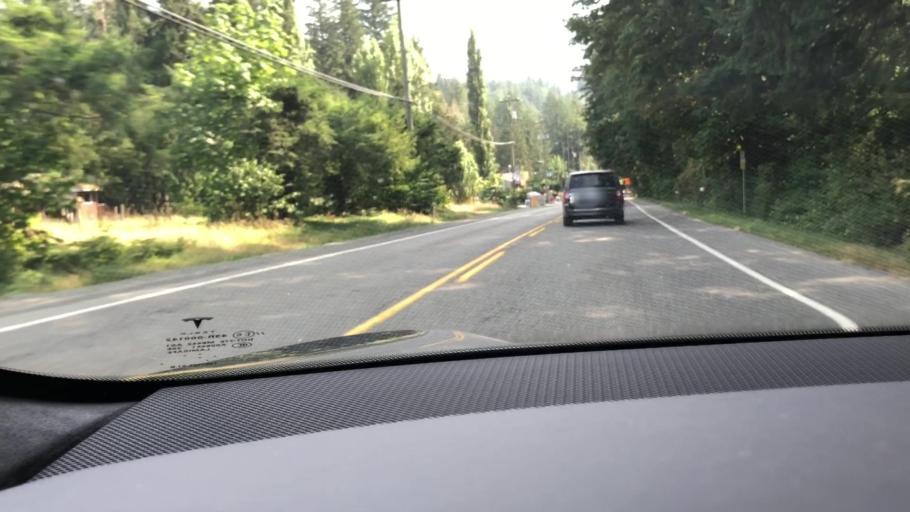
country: CA
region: British Columbia
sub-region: Fraser Valley Regional District
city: Chilliwack
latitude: 49.0721
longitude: -121.9624
